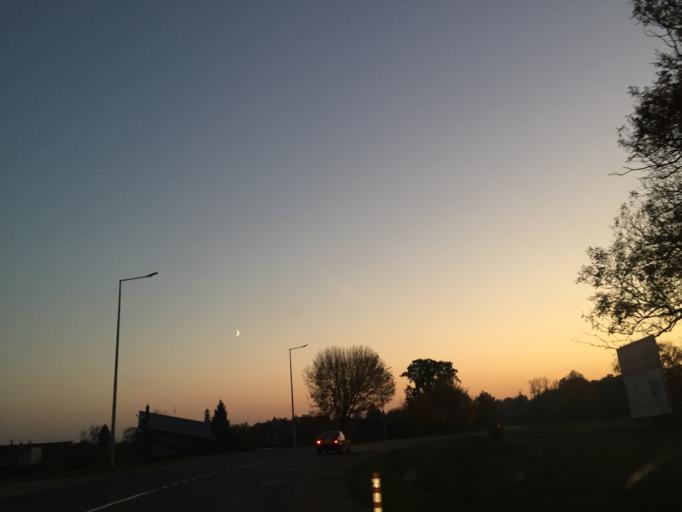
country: LT
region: Klaipedos apskritis
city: Kretinga
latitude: 55.9021
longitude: 21.2437
